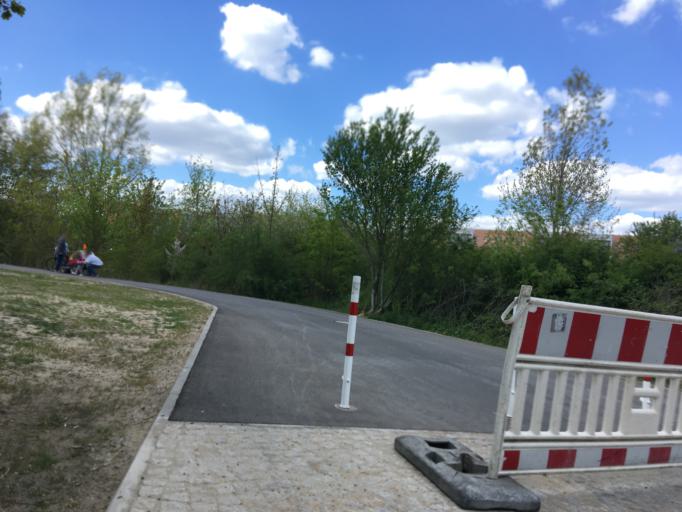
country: DE
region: Berlin
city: Hellersdorf
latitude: 52.5386
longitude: 13.6230
